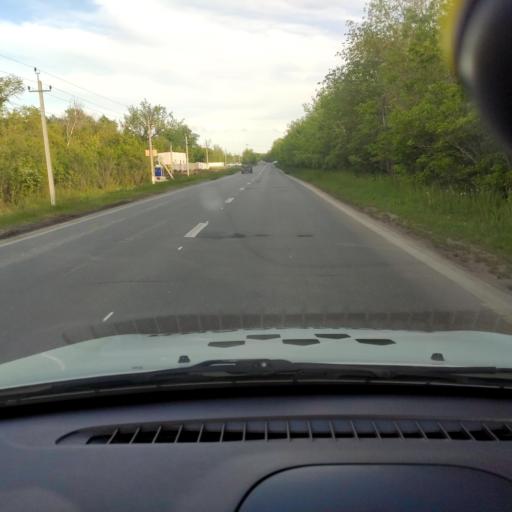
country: RU
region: Samara
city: Podstepki
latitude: 53.5895
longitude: 49.0499
